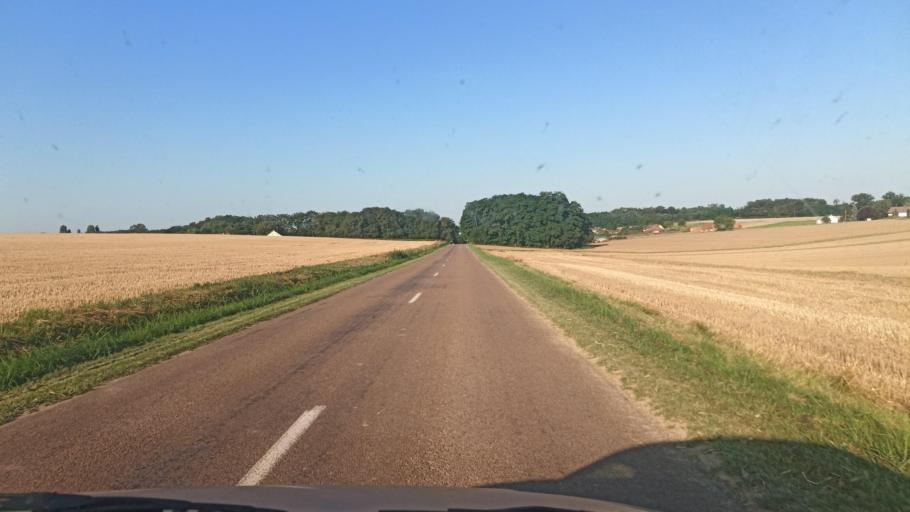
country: FR
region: Bourgogne
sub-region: Departement de l'Yonne
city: Saint-Valerien
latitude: 48.2353
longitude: 3.1272
